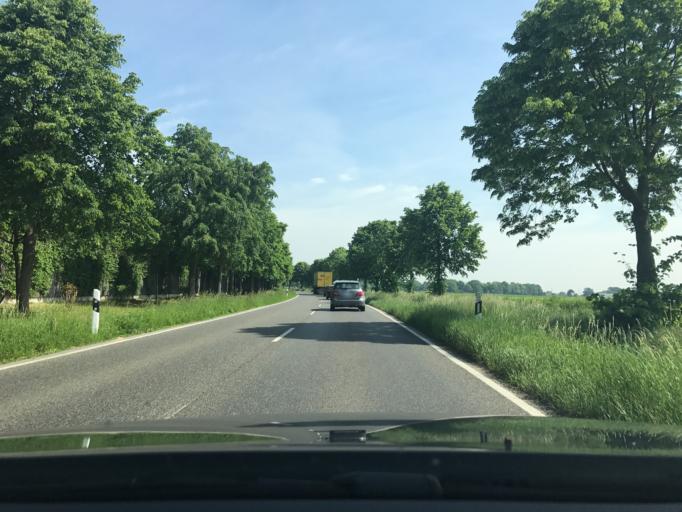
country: DE
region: North Rhine-Westphalia
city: Tonisvorst
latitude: 51.3045
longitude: 6.4355
